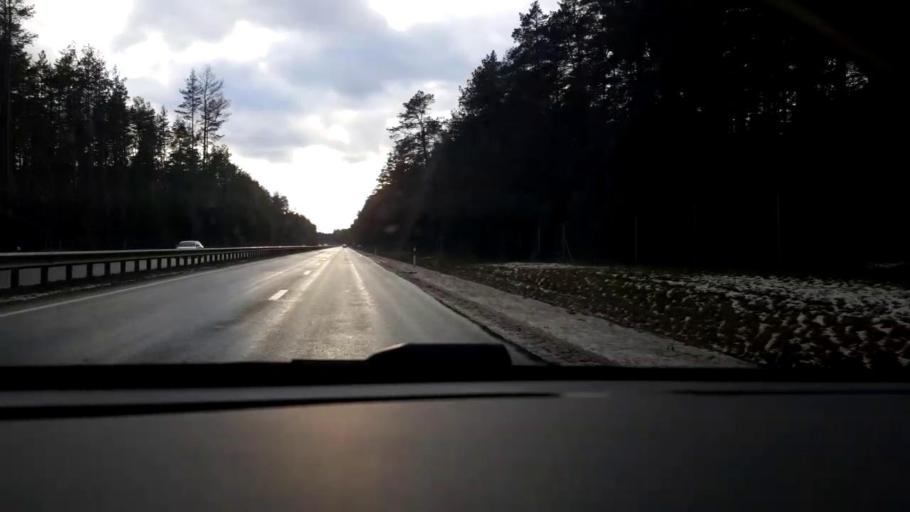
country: LT
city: Nemencine
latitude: 54.8235
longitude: 25.4389
